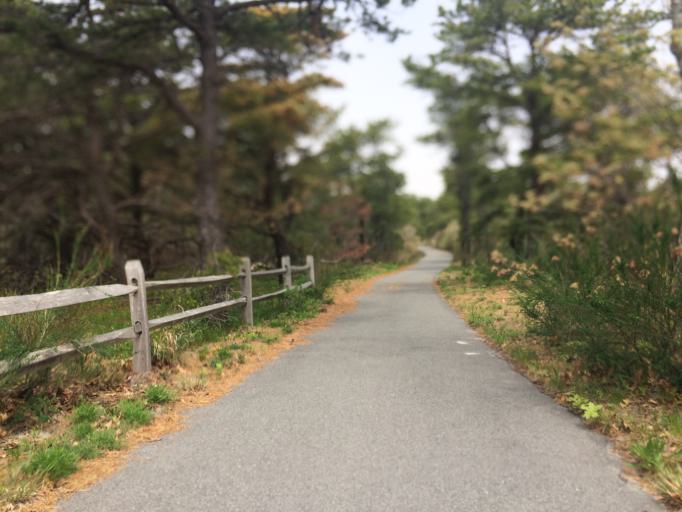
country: US
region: Massachusetts
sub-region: Barnstable County
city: Provincetown
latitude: 42.0748
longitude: -70.2090
